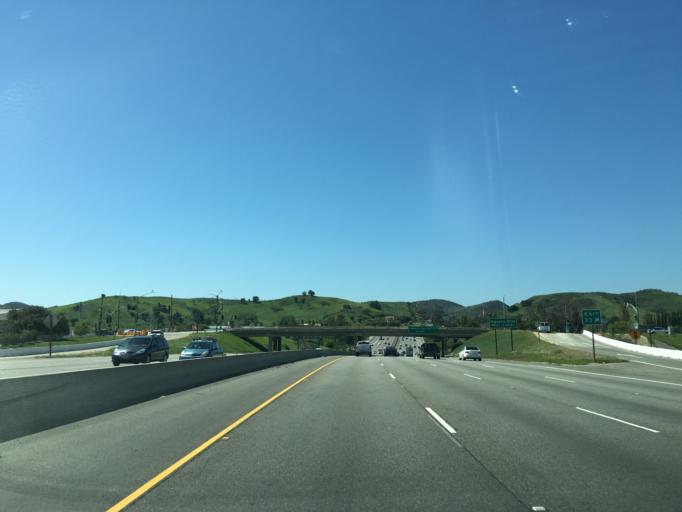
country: US
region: California
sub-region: Los Angeles County
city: Agoura
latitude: 34.1415
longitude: -118.7083
